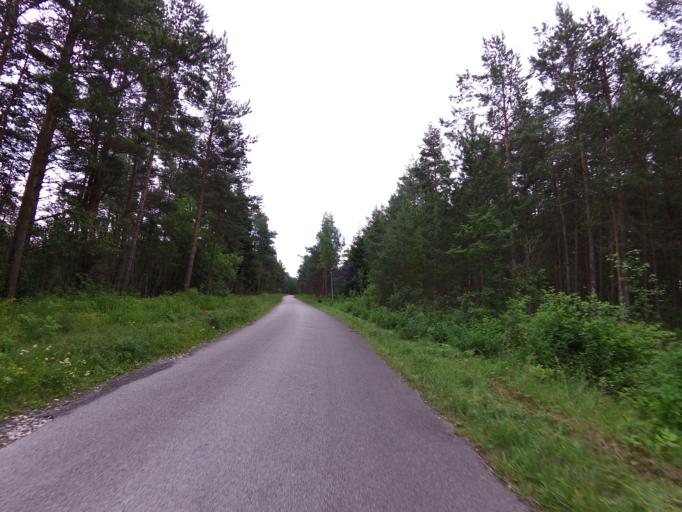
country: EE
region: Laeaene
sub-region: Vormsi vald
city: Hullo
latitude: 58.9809
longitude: 23.2506
